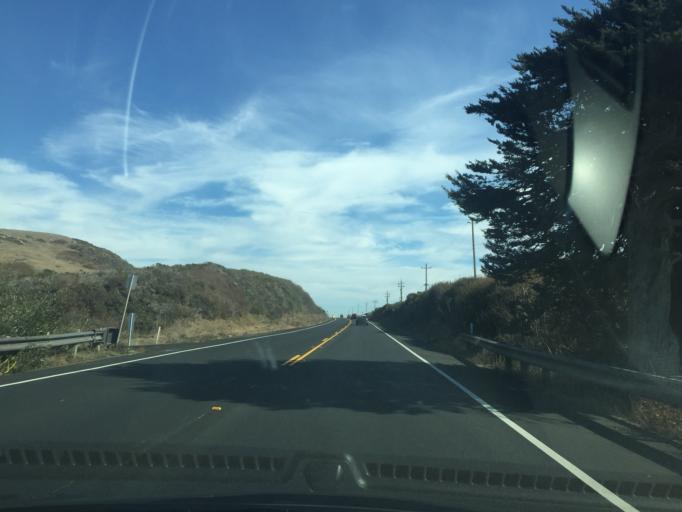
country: US
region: California
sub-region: Santa Cruz County
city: Bonny Doon
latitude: 36.9933
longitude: -122.1685
